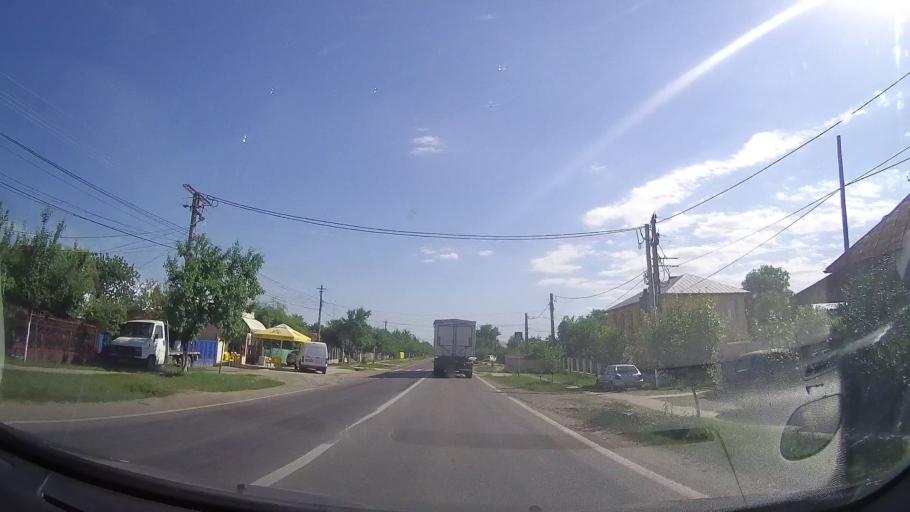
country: RO
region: Prahova
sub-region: Comuna Gura Vitioarei
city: Fagetu
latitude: 45.1238
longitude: 26.0351
